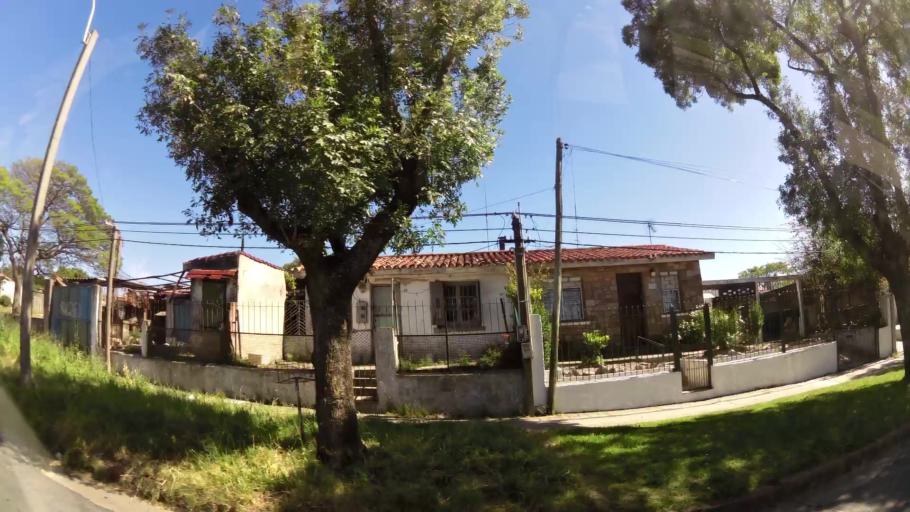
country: UY
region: Montevideo
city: Montevideo
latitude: -34.8692
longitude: -56.1263
